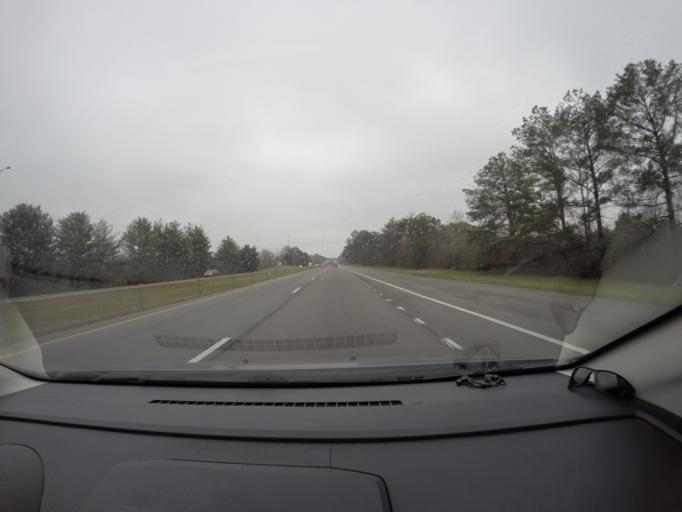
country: US
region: Tennessee
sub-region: Coffee County
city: Manchester
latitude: 35.4842
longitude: -86.0694
